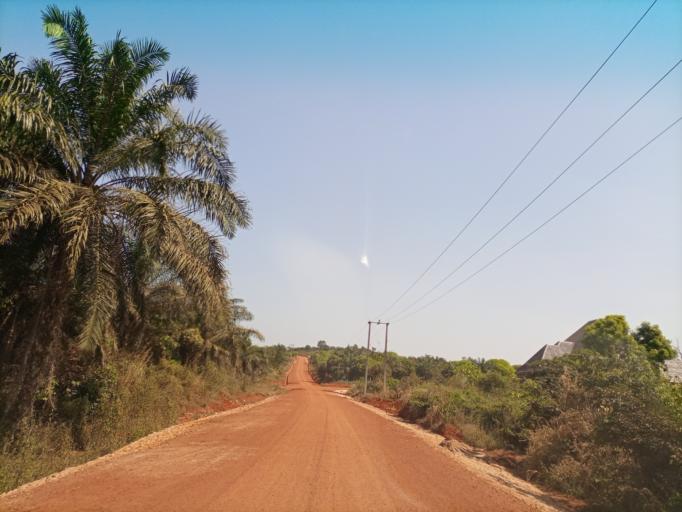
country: NG
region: Enugu
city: Nsukka
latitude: 6.8007
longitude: 7.3406
